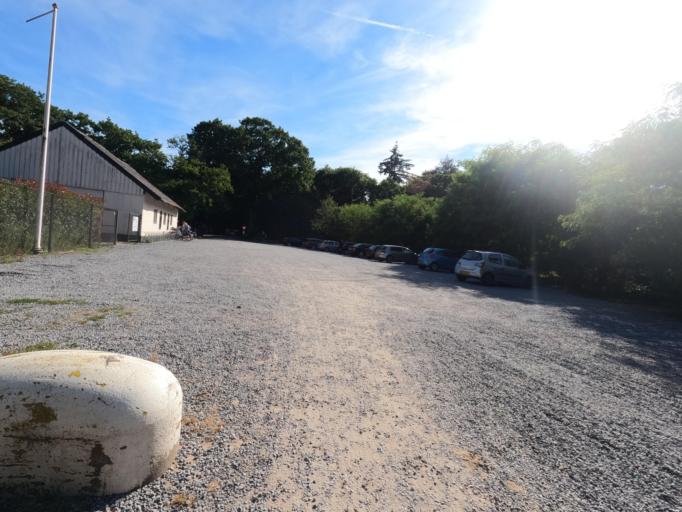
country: NL
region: Limburg
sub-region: Gemeente Beesel
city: Beesel
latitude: 51.2336
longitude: 6.0689
